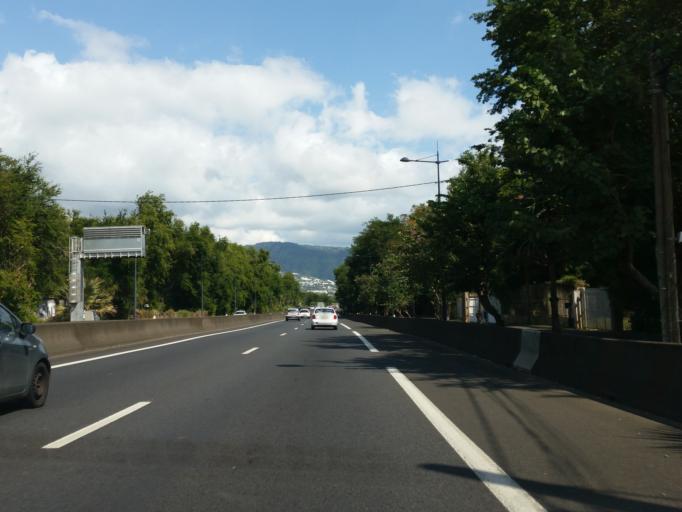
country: RE
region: Reunion
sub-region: Reunion
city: Saint-Denis
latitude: -20.8858
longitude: 55.4959
